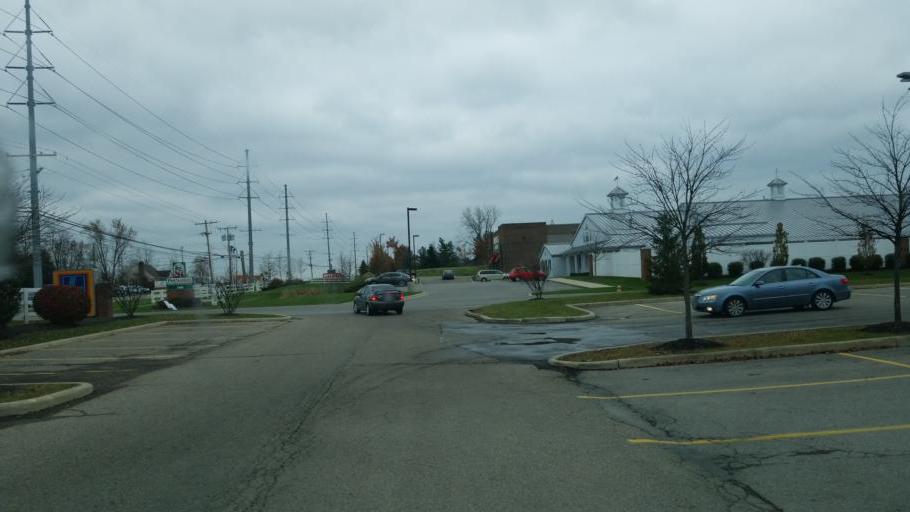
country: US
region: Ohio
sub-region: Franklin County
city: Gahanna
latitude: 40.0694
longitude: -82.8632
